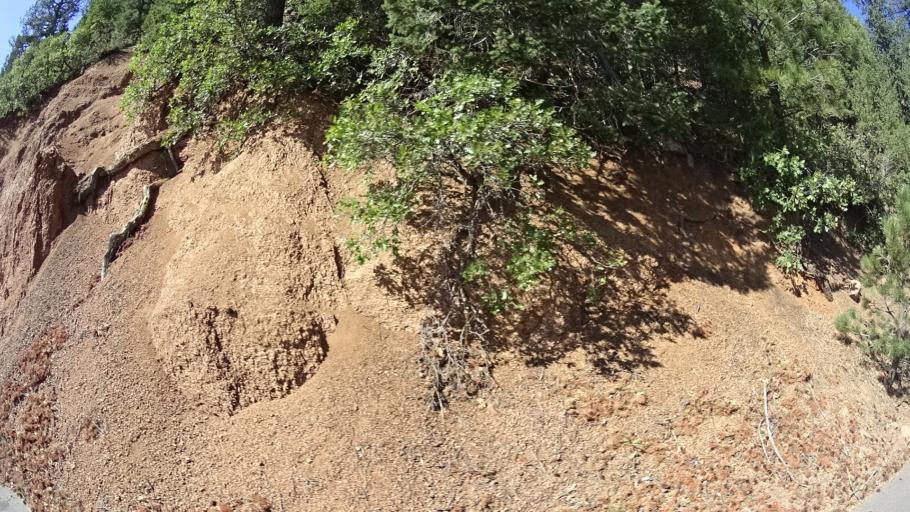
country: US
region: Colorado
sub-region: El Paso County
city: Colorado Springs
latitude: 38.8015
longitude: -104.8770
